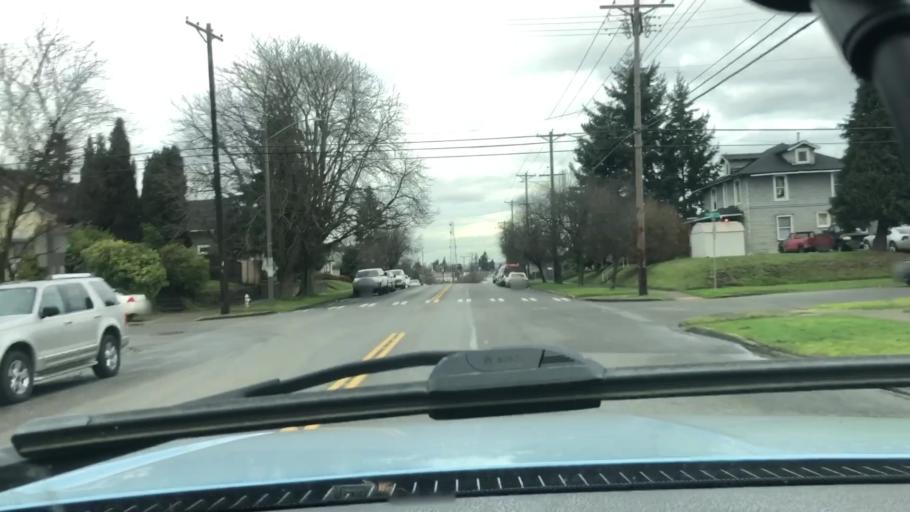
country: US
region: Washington
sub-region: Pierce County
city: Tacoma
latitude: 47.2262
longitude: -122.4208
